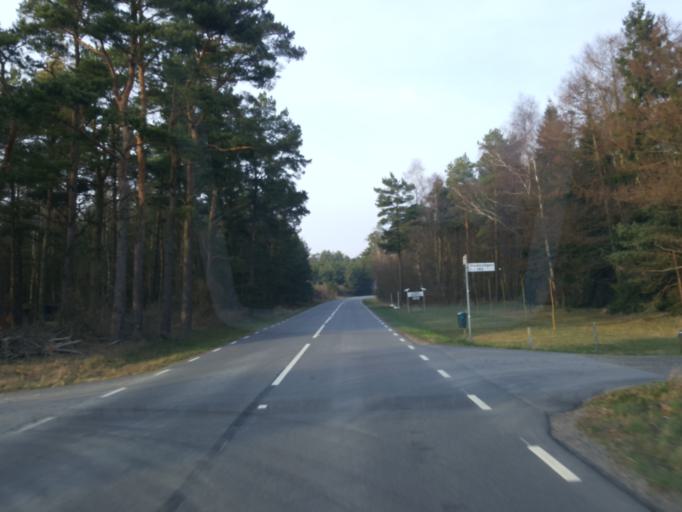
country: SE
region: Skane
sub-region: Simrishamns Kommun
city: Simrishamn
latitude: 55.4055
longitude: 14.1872
